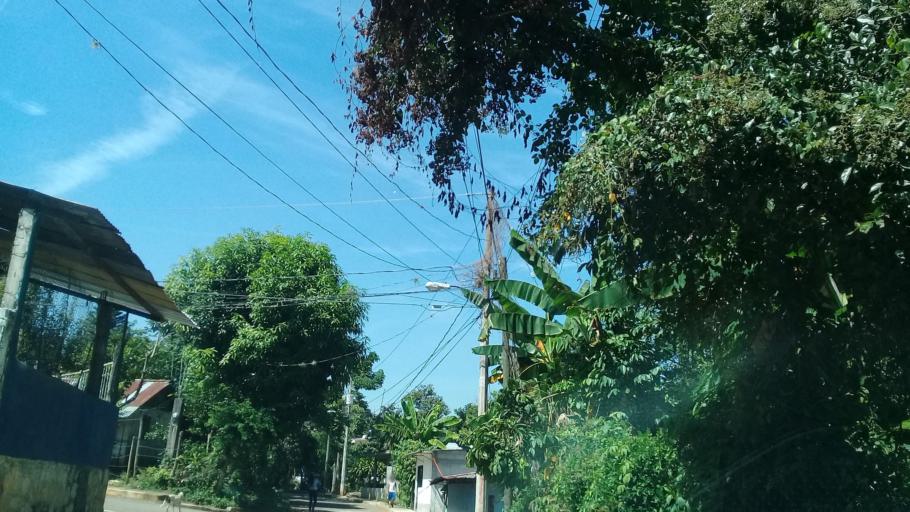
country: MX
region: Veracruz
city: Amatlan de los Reyes
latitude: 18.8415
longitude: -96.9156
